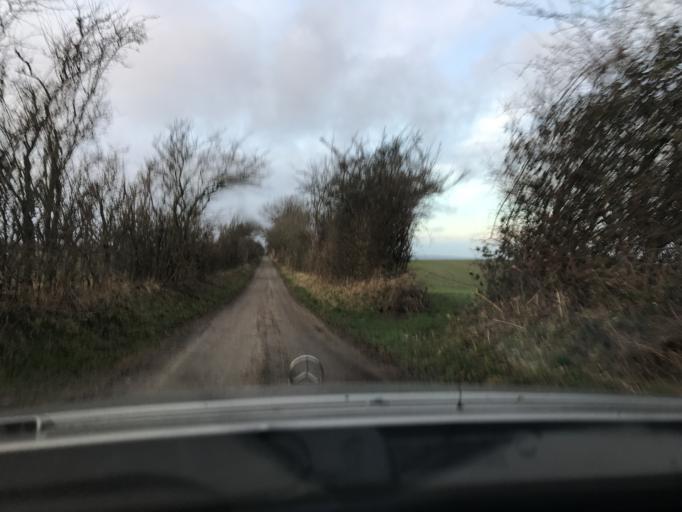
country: DK
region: South Denmark
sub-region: Sonderborg Kommune
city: Nordborg
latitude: 55.0574
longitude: 9.6719
